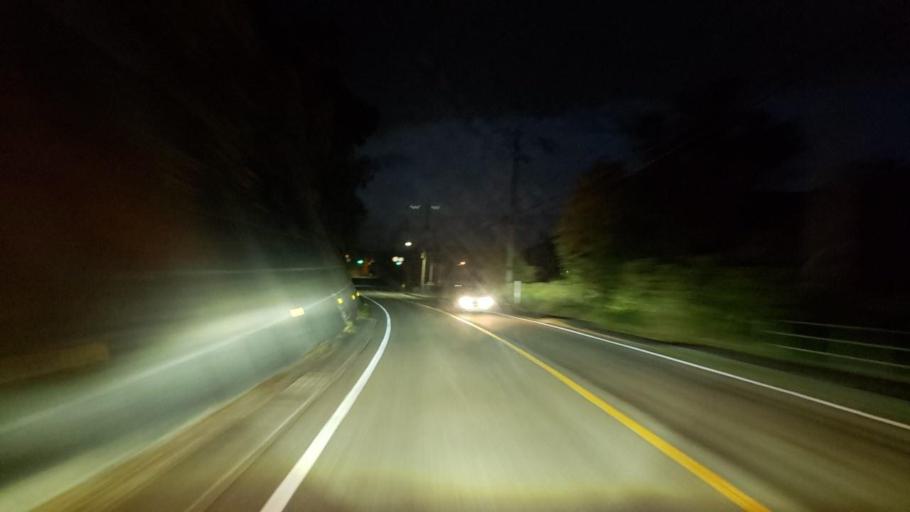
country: JP
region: Tokushima
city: Narutocho-mitsuishi
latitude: 34.2063
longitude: 134.5707
